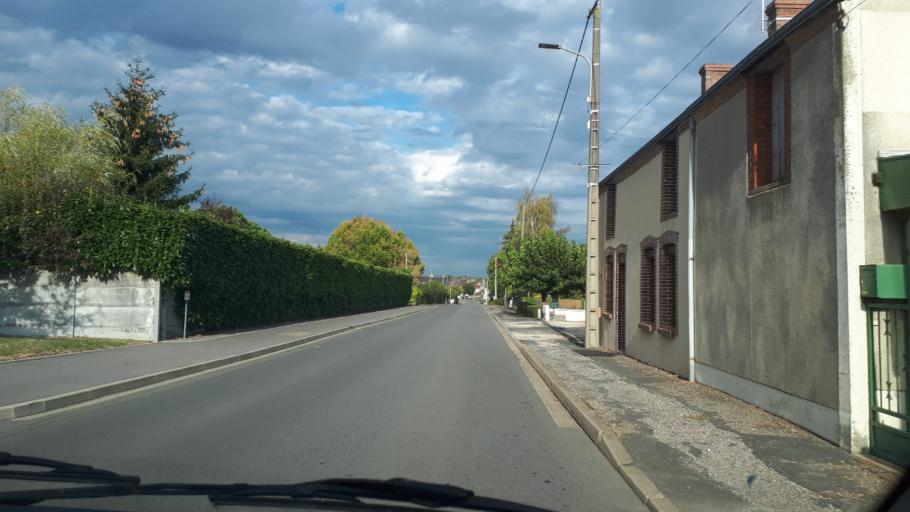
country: FR
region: Centre
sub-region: Departement du Loir-et-Cher
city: Mondoubleau
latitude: 47.9779
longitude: 0.9017
